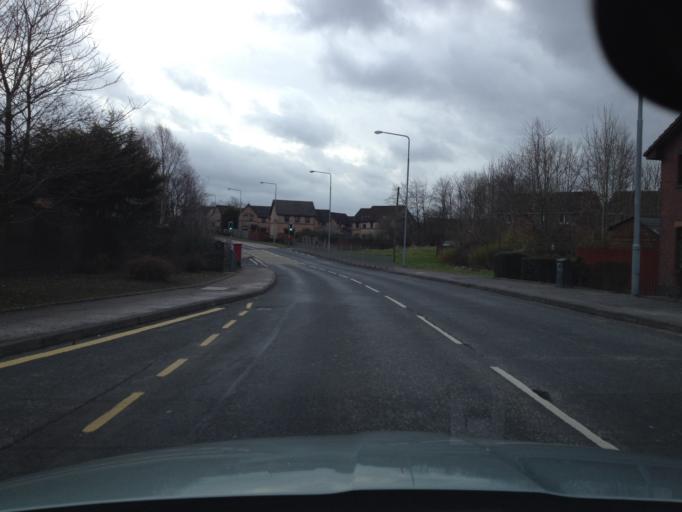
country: GB
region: Scotland
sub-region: West Lothian
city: Livingston
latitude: 55.9009
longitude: -3.5297
